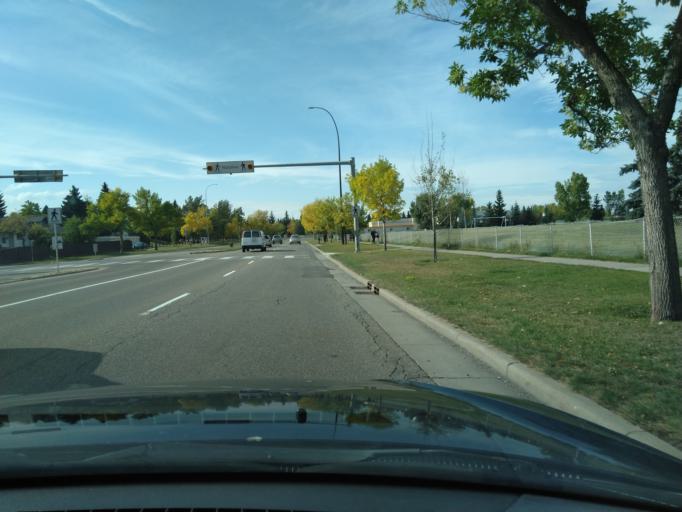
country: CA
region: Alberta
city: Calgary
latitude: 51.1300
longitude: -114.0831
